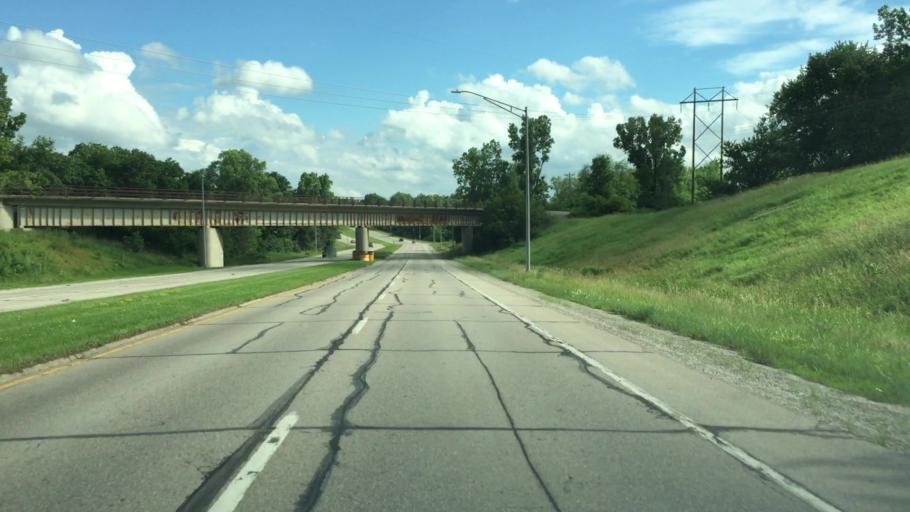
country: US
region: Iowa
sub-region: Jasper County
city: Newton
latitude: 41.6960
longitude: -93.0766
